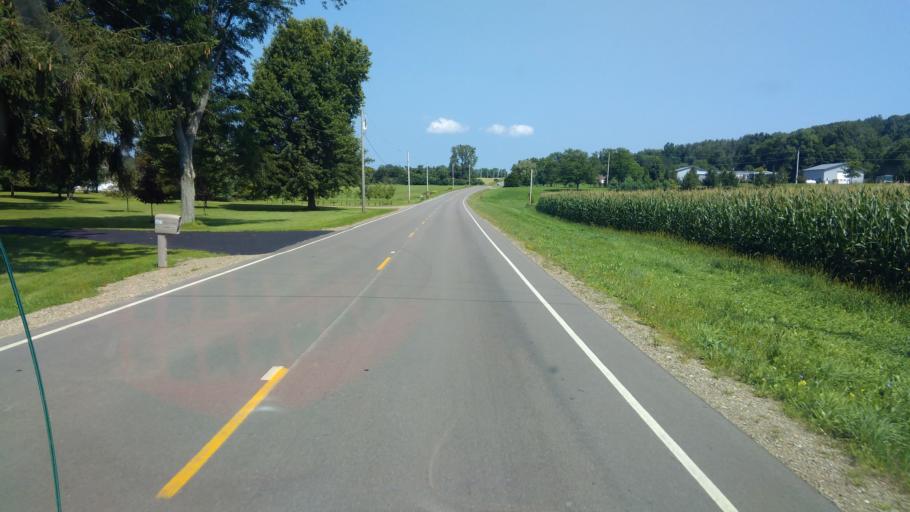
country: US
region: New York
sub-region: Allegany County
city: Belmont
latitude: 42.2460
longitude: -78.0407
